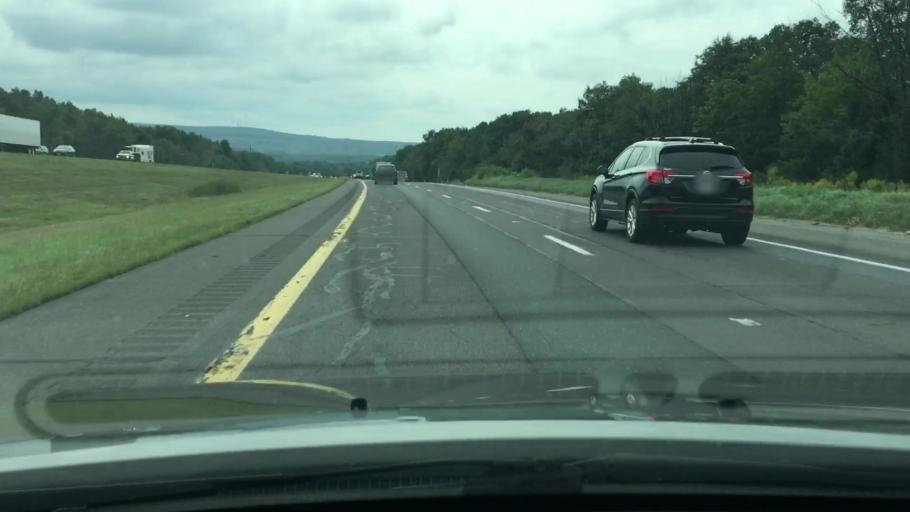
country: US
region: Pennsylvania
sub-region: Schuylkill County
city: Tremont
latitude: 40.6437
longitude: -76.4278
